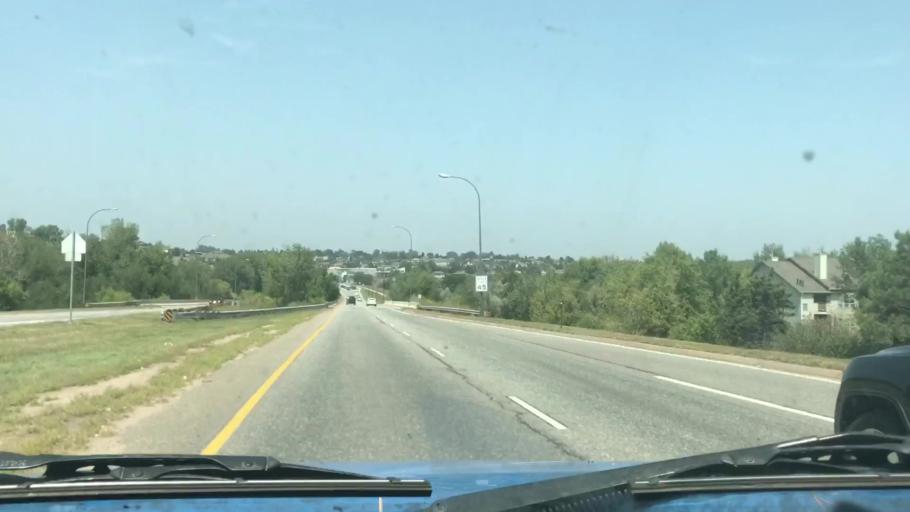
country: US
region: Colorado
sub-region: Jefferson County
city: Lakewood
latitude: 39.6609
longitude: -105.1124
